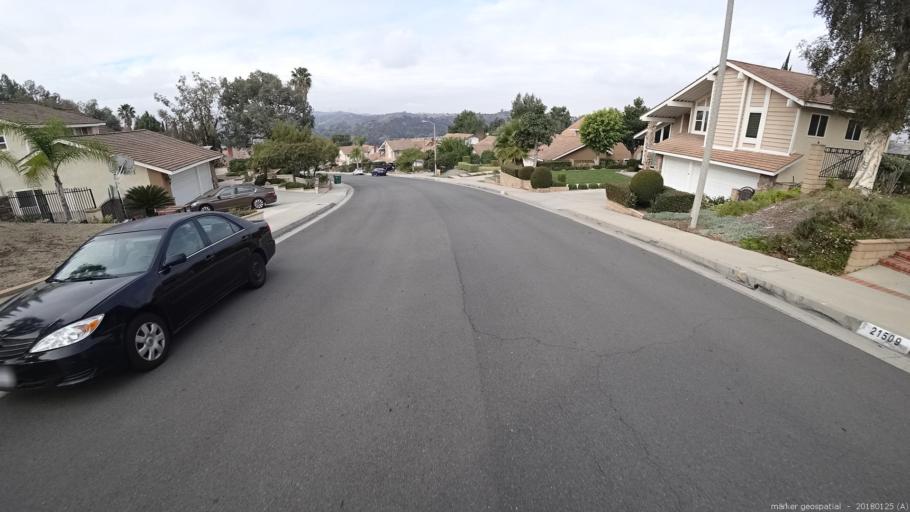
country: US
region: California
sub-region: Los Angeles County
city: Walnut
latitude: 33.9648
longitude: -117.8400
